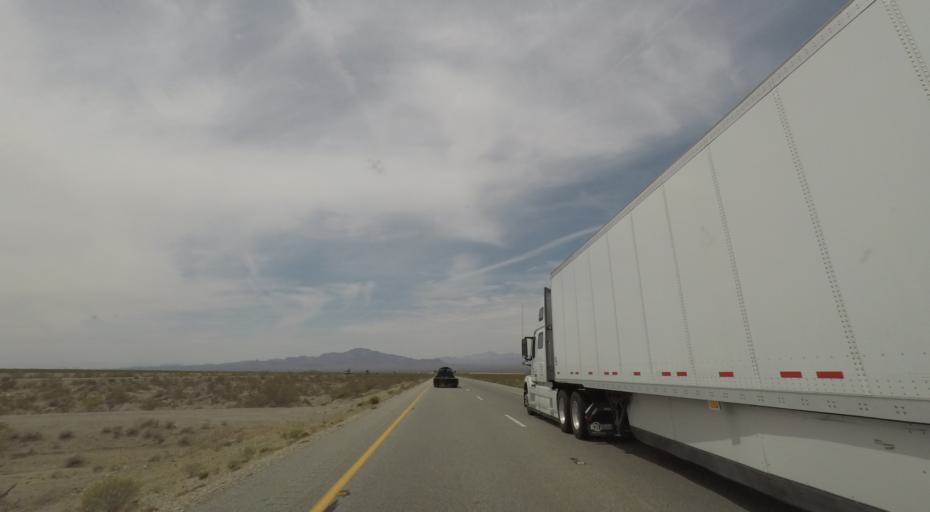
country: US
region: California
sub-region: San Bernardino County
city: Needles
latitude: 34.8189
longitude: -115.1391
